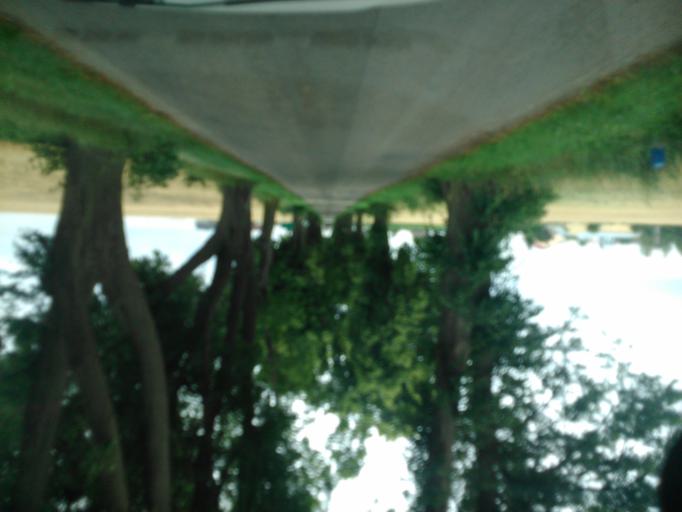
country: PL
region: Kujawsko-Pomorskie
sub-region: Powiat brodnicki
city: Brodnica
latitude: 53.2474
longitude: 19.3385
